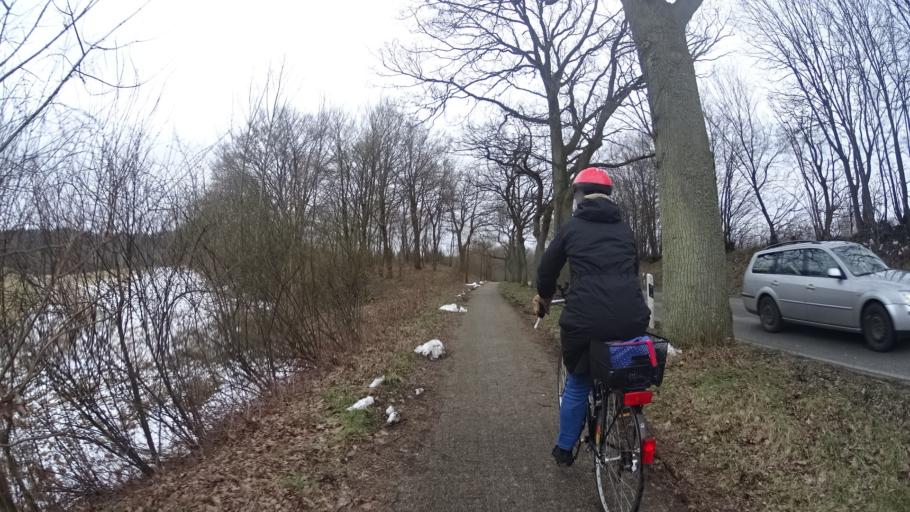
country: DE
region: Schleswig-Holstein
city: Neukirchen
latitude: 54.1954
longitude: 10.5626
